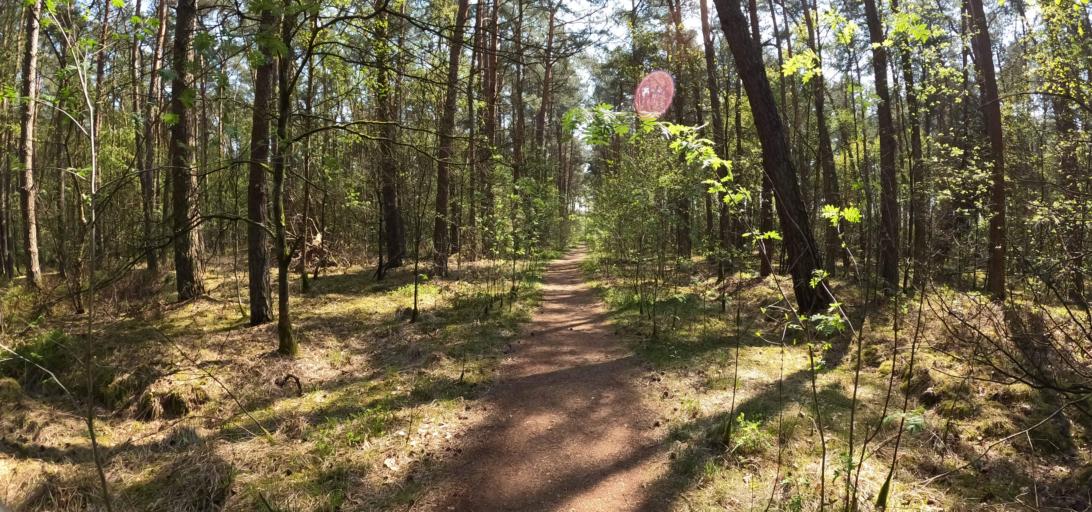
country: BE
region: Flanders
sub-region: Provincie Antwerpen
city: Lille
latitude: 51.2746
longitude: 4.8199
